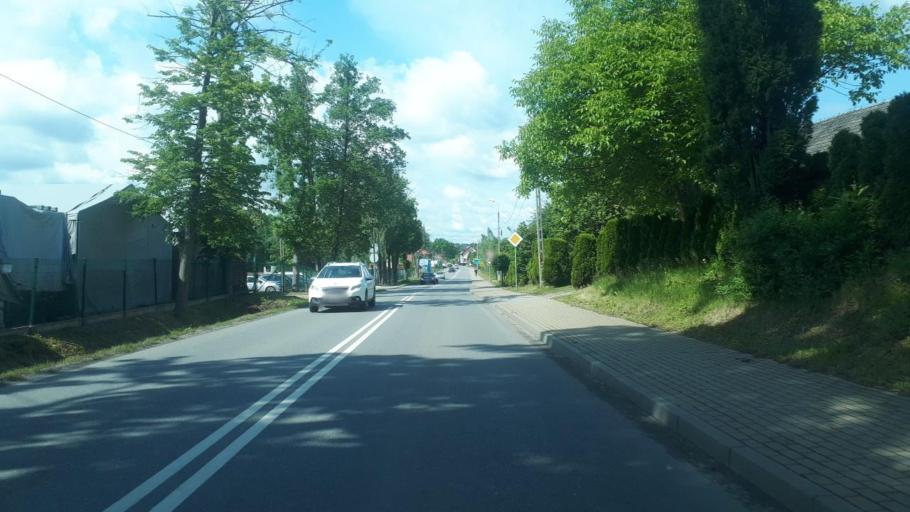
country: PL
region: Silesian Voivodeship
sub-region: Powiat bielski
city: Wilamowice
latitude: 49.9278
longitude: 19.1149
